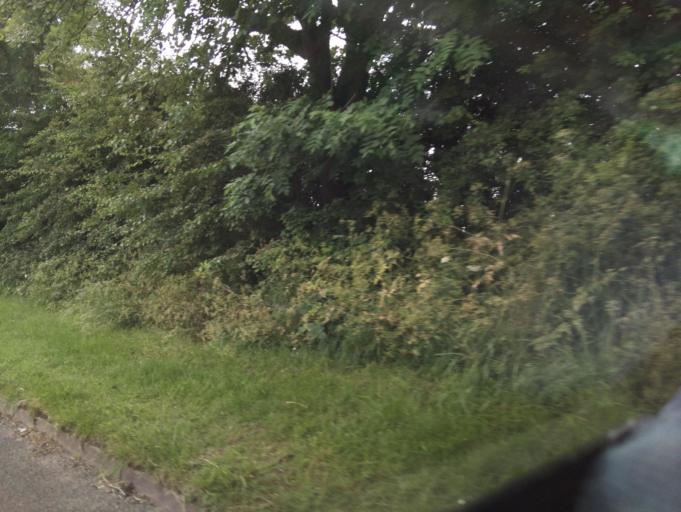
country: GB
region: England
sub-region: Leicestershire
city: Coalville
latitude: 52.7345
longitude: -1.3514
